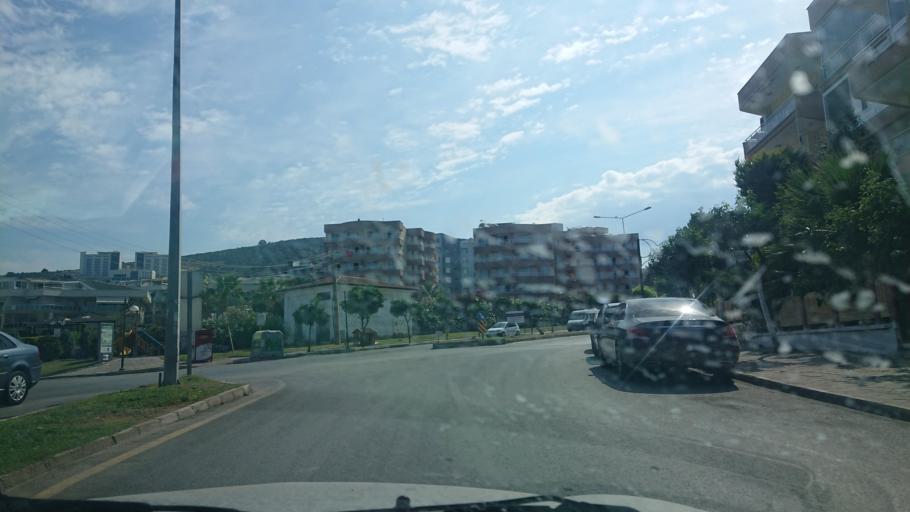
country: TR
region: Aydin
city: Kusadasi
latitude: 37.8659
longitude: 27.2711
